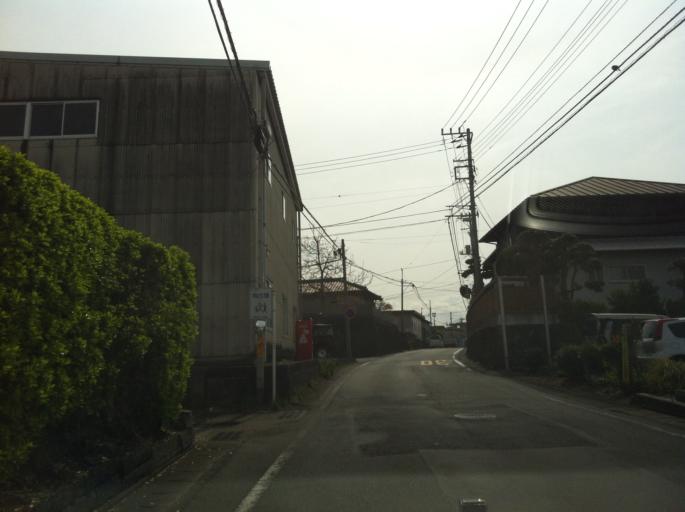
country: JP
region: Shizuoka
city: Numazu
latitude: 35.1417
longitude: 138.8018
